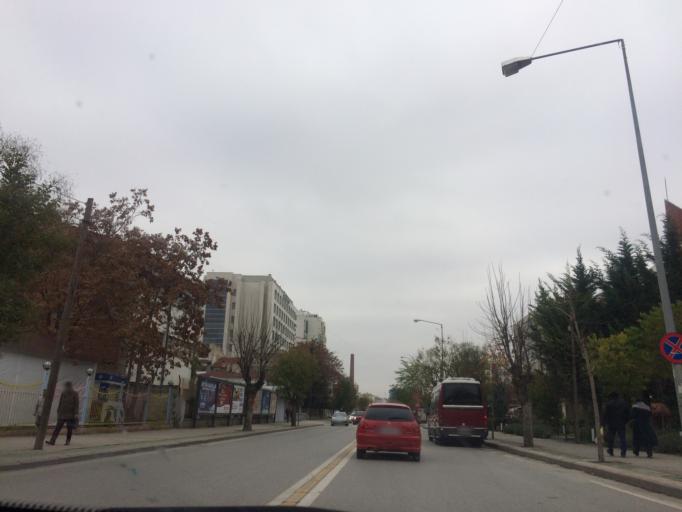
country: TR
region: Eskisehir
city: Eskisehir
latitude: 39.7837
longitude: 30.5043
